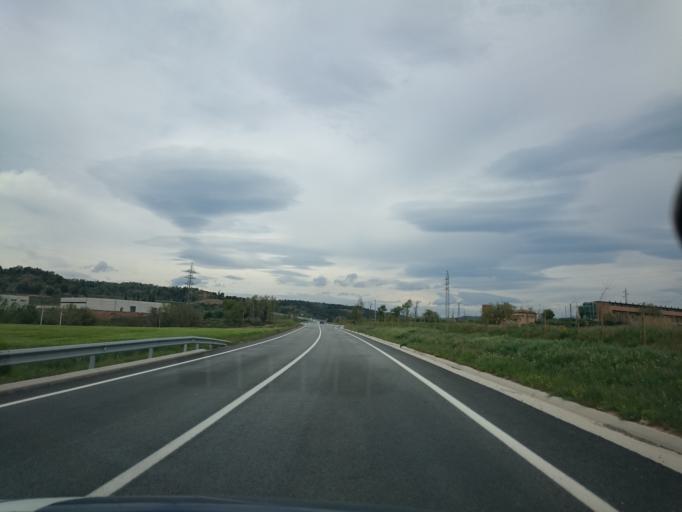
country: ES
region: Catalonia
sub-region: Provincia de Barcelona
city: Olost
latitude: 41.9879
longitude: 2.1026
